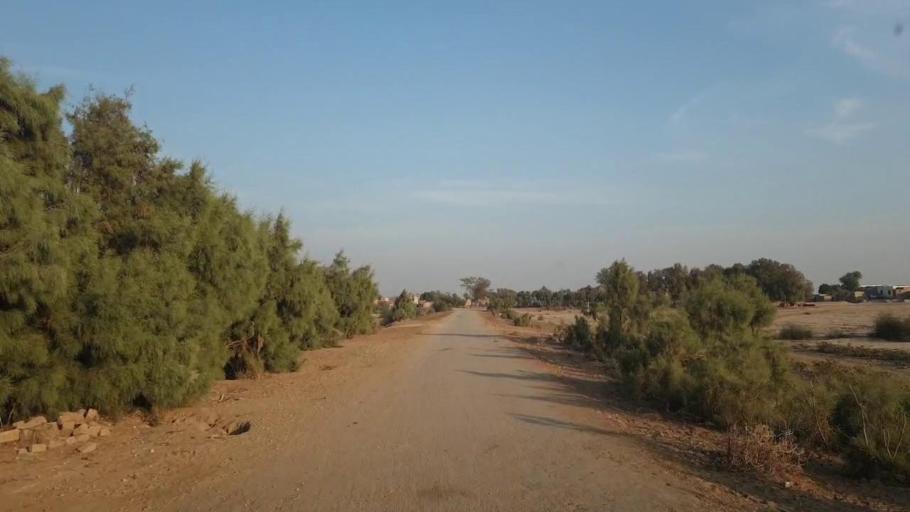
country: PK
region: Sindh
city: Sann
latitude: 25.9223
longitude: 68.1898
